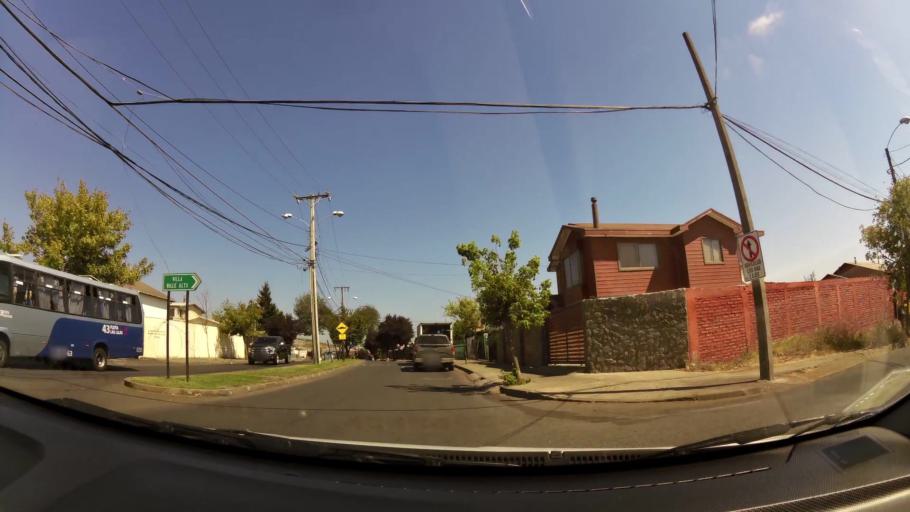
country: CL
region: Biobio
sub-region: Provincia de Concepcion
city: Concepcion
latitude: -36.7871
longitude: -73.0431
